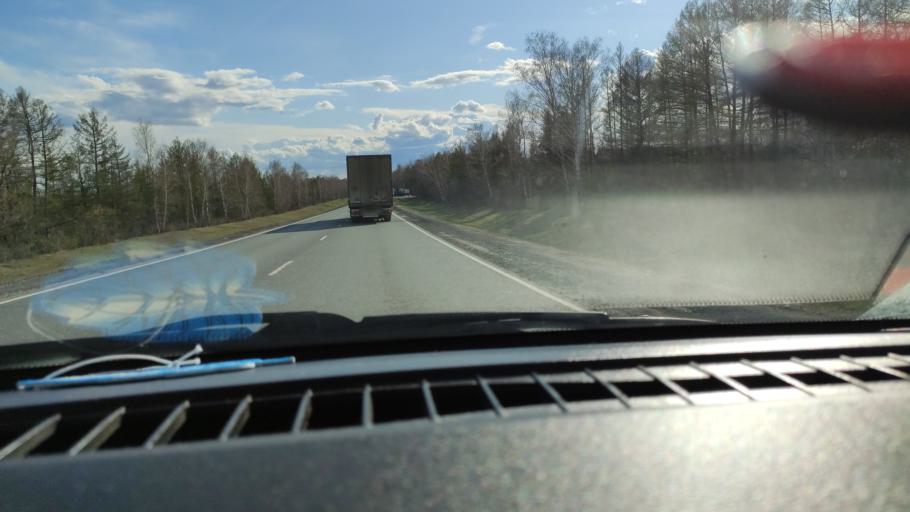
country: RU
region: Saratov
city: Sennoy
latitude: 52.1270
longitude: 46.8555
